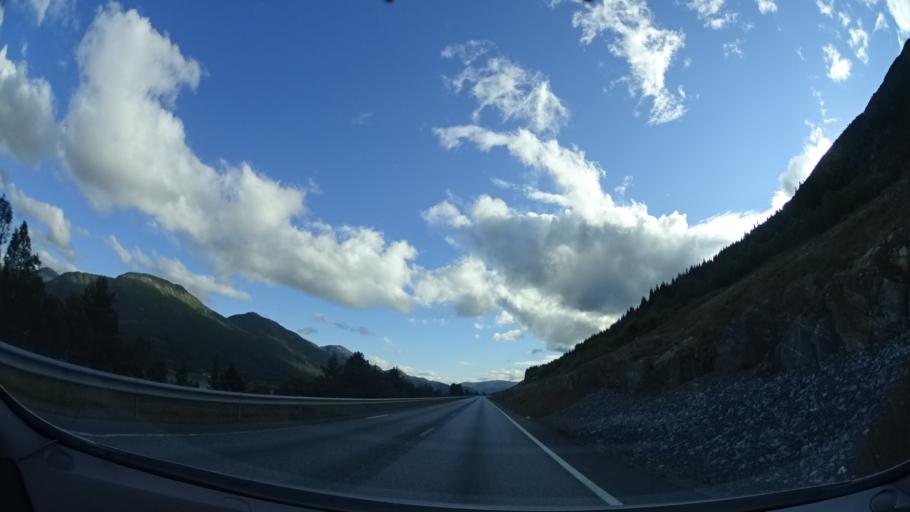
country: NO
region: More og Romsdal
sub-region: Gjemnes
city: Batnfjordsora
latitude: 62.9352
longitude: 7.7307
